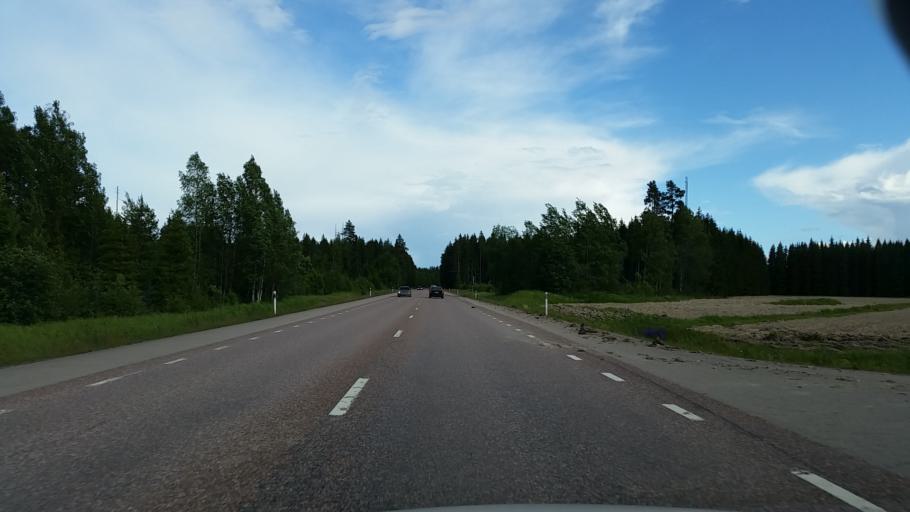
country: SE
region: Dalarna
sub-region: Smedjebackens Kommun
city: Smedjebacken
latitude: 60.1135
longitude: 15.4822
